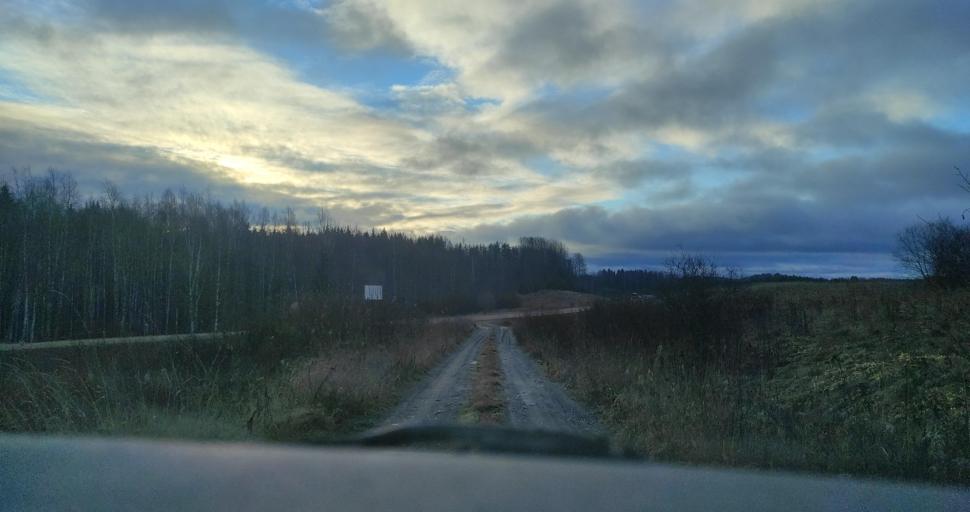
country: RU
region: Republic of Karelia
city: Pitkyaranta
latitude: 61.7265
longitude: 31.3839
